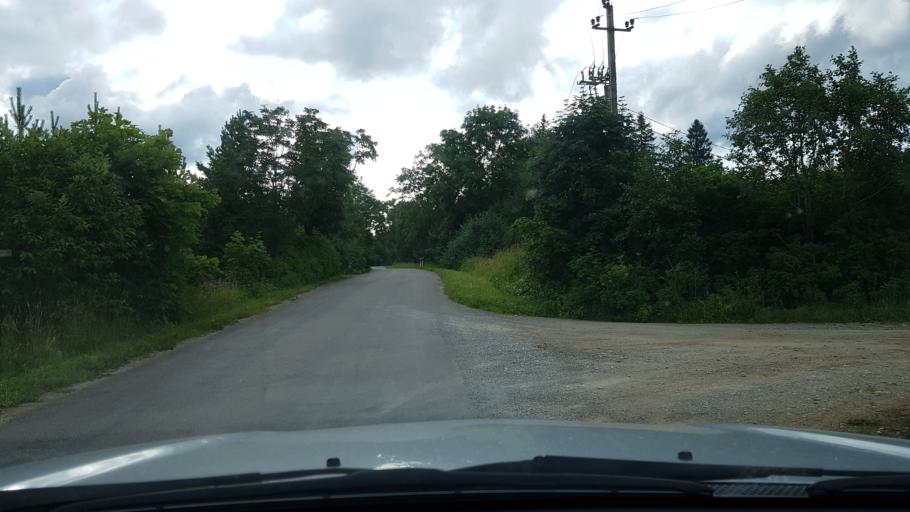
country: EE
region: Ida-Virumaa
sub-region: Narva-Joesuu linn
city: Narva-Joesuu
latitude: 59.4093
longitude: 27.9835
